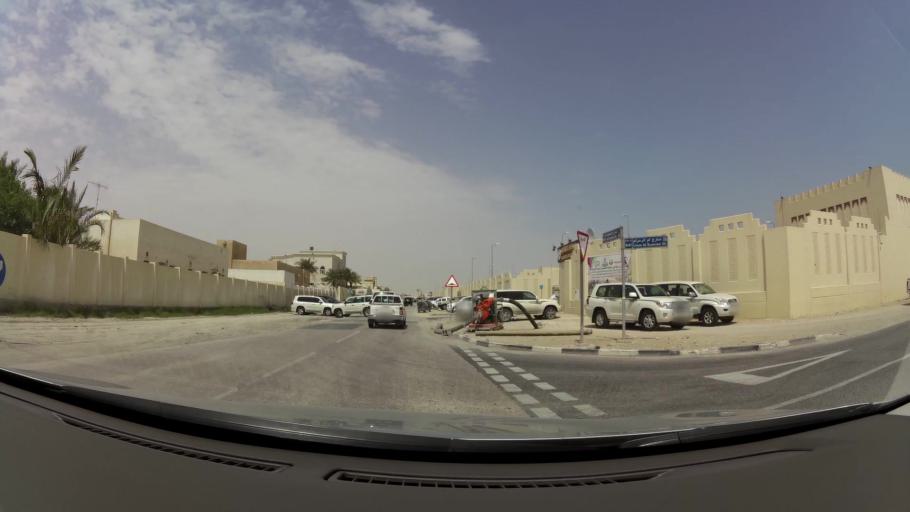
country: QA
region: Baladiyat ar Rayyan
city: Ar Rayyan
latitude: 25.3521
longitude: 51.4764
